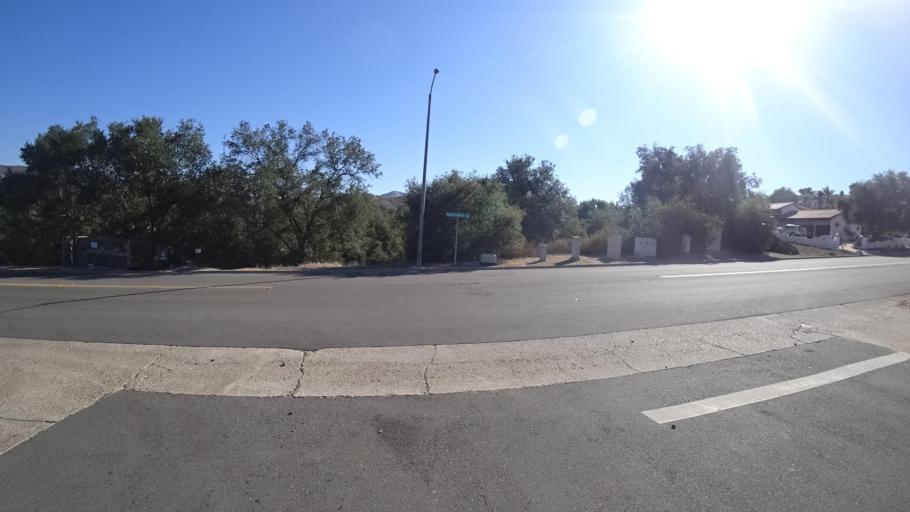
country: US
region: California
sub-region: San Diego County
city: San Diego Country Estates
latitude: 33.0035
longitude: -116.8194
